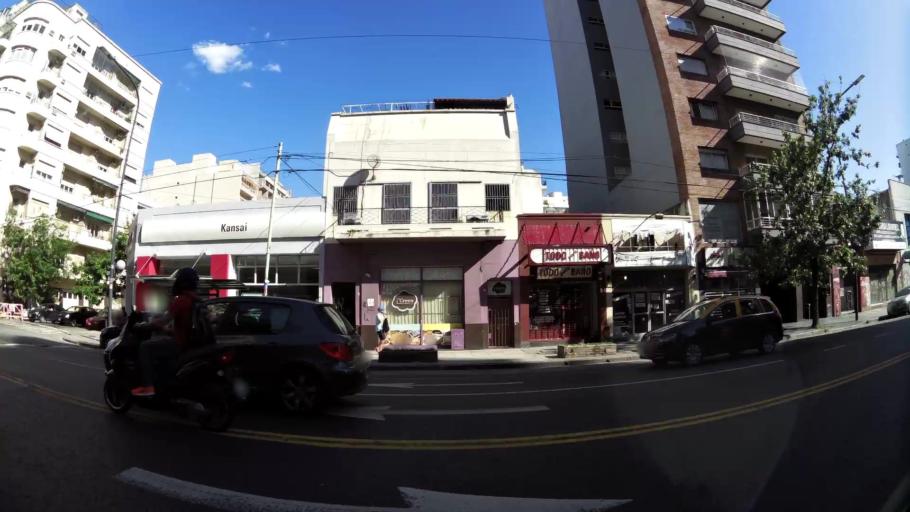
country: AR
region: Buenos Aires F.D.
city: Villa Santa Rita
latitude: -34.6250
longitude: -58.4523
